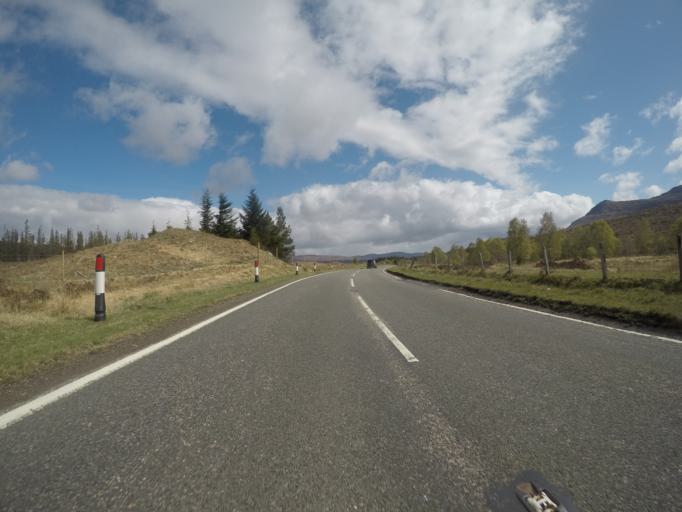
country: GB
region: Scotland
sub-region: Highland
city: Spean Bridge
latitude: 57.1333
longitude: -4.9573
